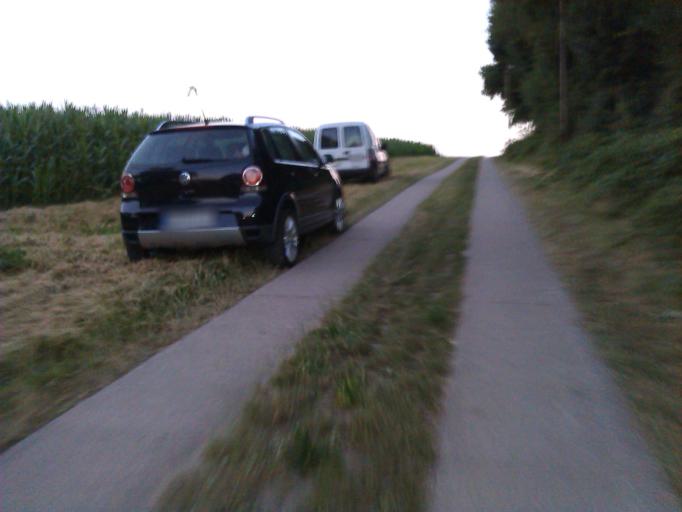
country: DE
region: Baden-Wuerttemberg
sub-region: Regierungsbezirk Stuttgart
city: Oedheim
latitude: 49.2545
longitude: 9.2342
